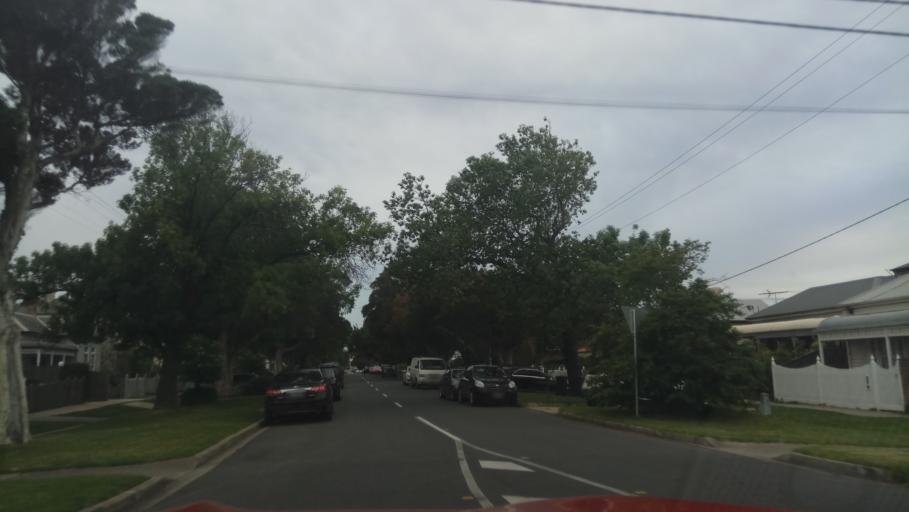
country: AU
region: Victoria
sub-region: Hobsons Bay
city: Williamstown
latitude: -37.8673
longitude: 144.9004
